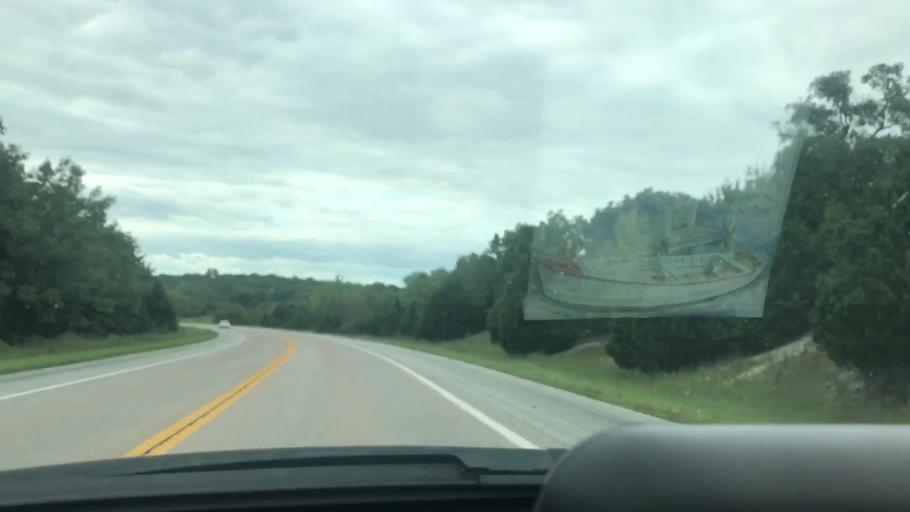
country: US
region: Missouri
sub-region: Benton County
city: Warsaw
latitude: 38.2047
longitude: -93.3268
